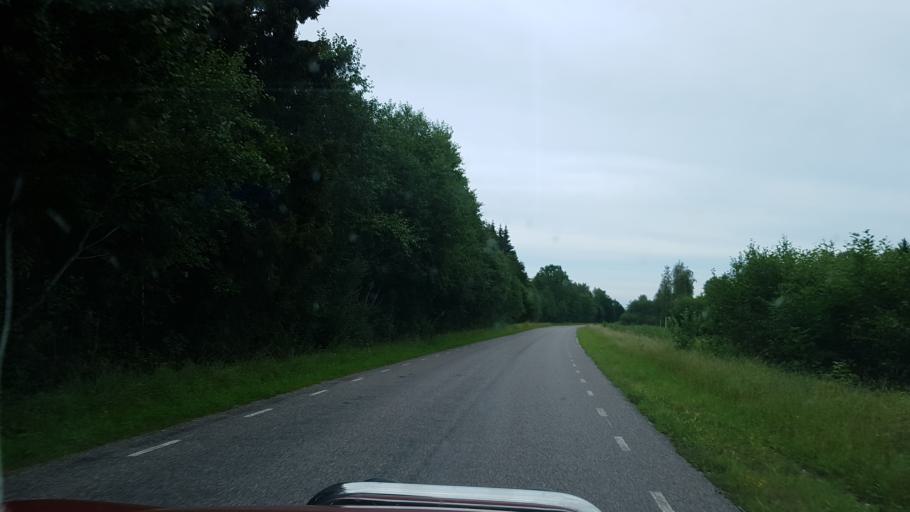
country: EE
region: Laeaene
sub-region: Lihula vald
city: Lihula
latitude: 58.8774
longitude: 23.8114
